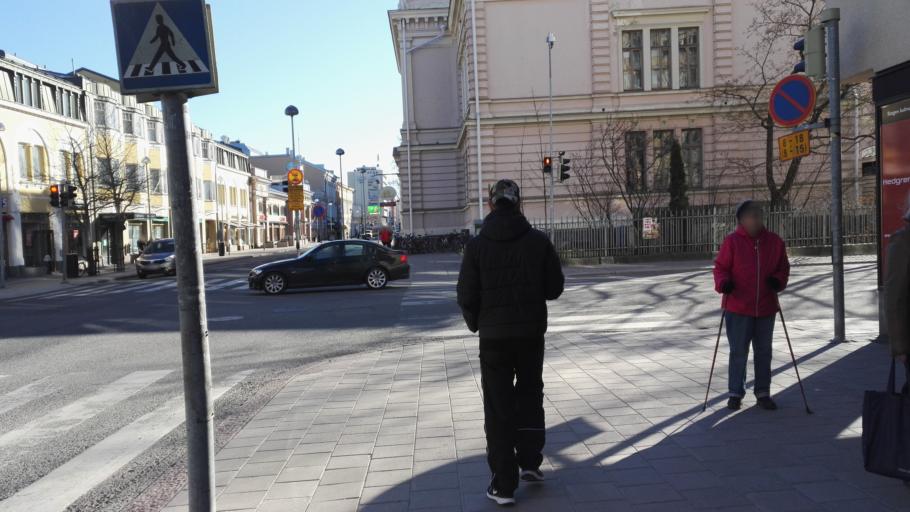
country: FI
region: Varsinais-Suomi
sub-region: Turku
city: Turku
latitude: 60.4497
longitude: 22.2633
